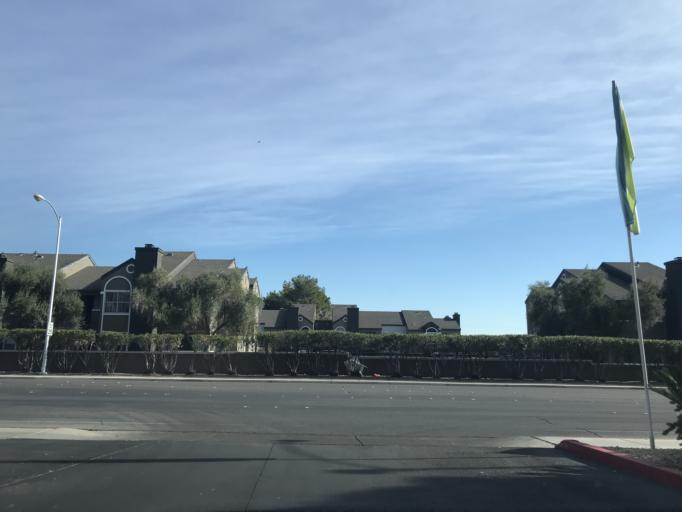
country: US
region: Nevada
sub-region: Clark County
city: Spring Valley
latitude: 36.0975
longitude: -115.2168
